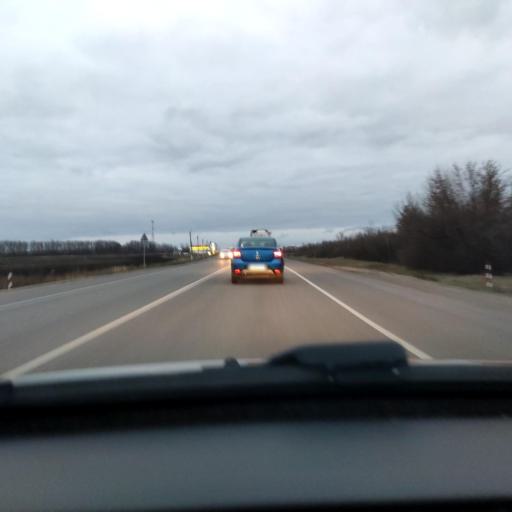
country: RU
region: Lipetsk
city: Borinskoye
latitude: 52.4590
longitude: 39.3199
